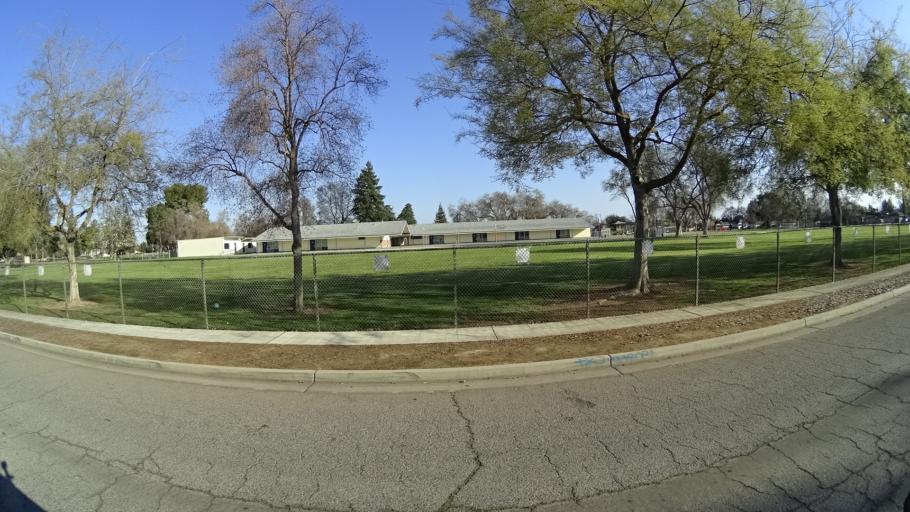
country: US
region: California
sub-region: Fresno County
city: Fresno
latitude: 36.8175
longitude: -119.7784
